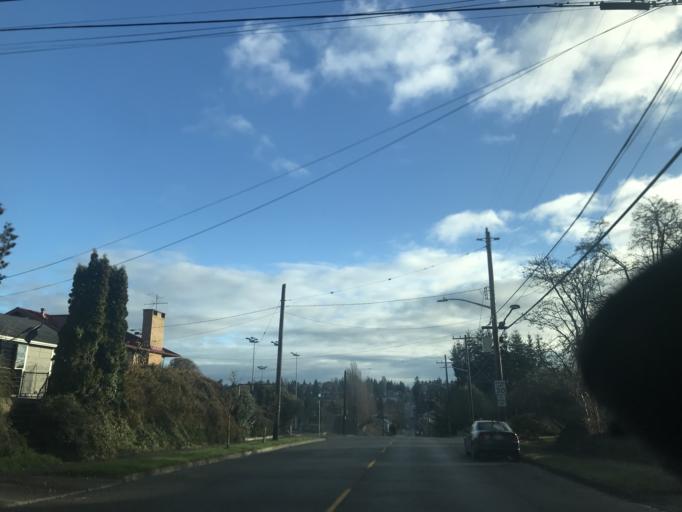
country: US
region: Washington
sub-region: King County
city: White Center
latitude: 47.5247
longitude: -122.3710
